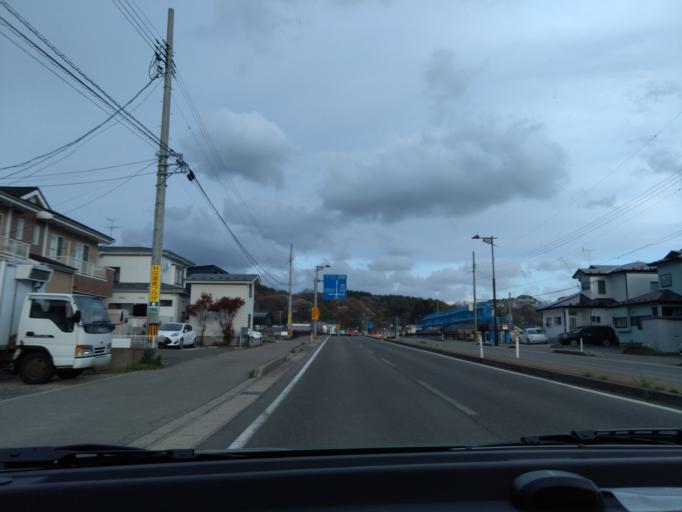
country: JP
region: Akita
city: Akita
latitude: 39.7479
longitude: 140.1282
